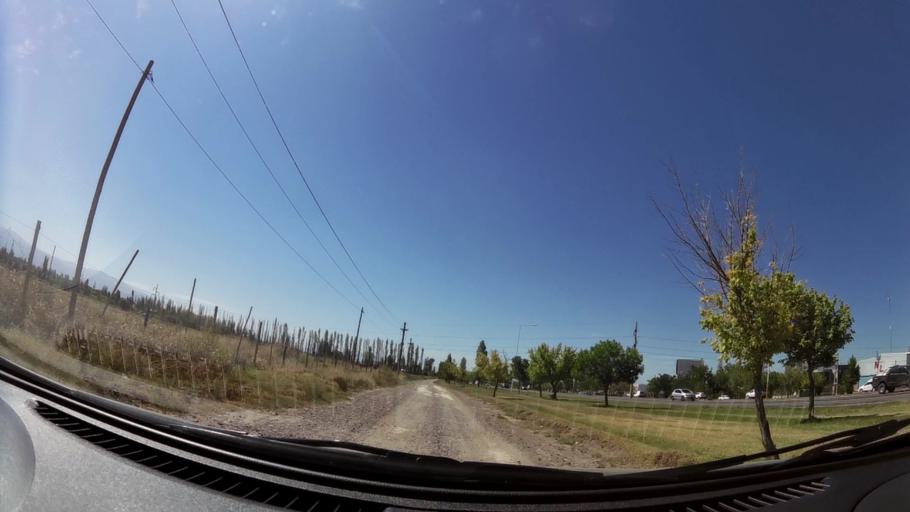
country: AR
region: Mendoza
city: Lujan de Cuyo
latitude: -32.9895
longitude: -68.8517
